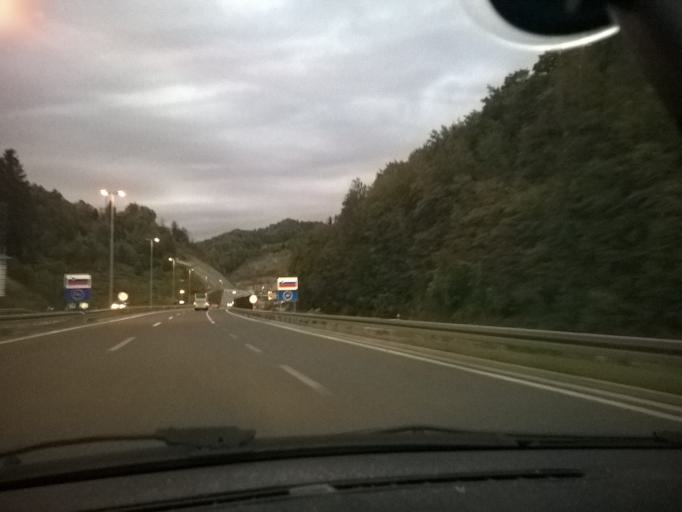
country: SI
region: Zetale
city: Zetale
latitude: 46.2706
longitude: 15.8676
